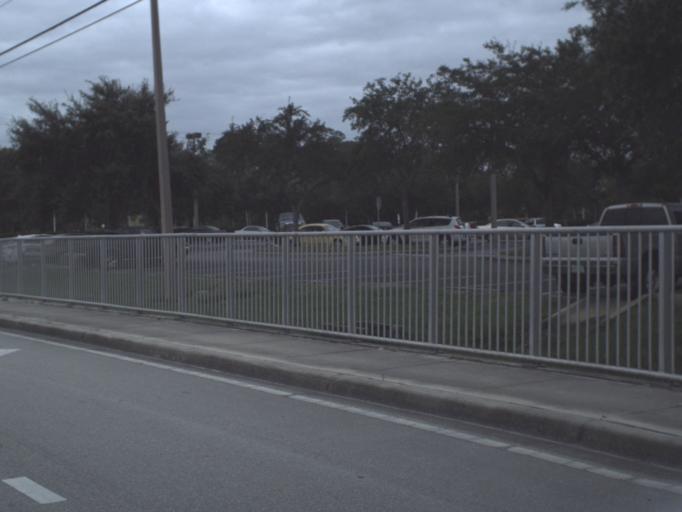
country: US
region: Florida
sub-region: Collier County
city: Lely Resort
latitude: 26.1107
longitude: -81.6873
